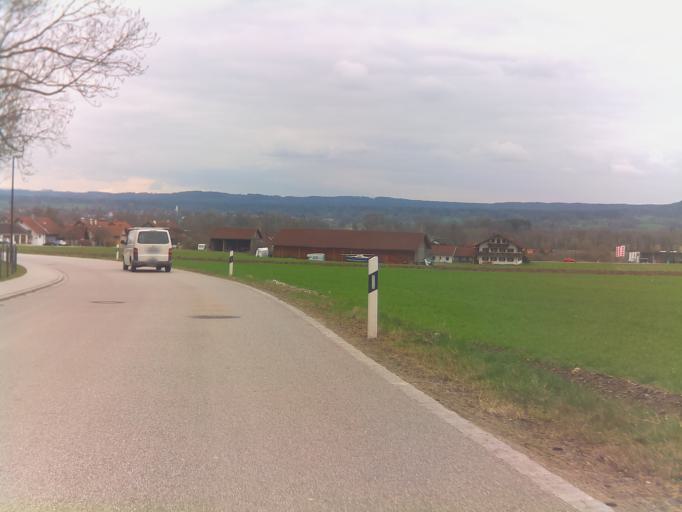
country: DE
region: Bavaria
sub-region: Upper Bavaria
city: Pahl
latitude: 47.9303
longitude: 11.1611
